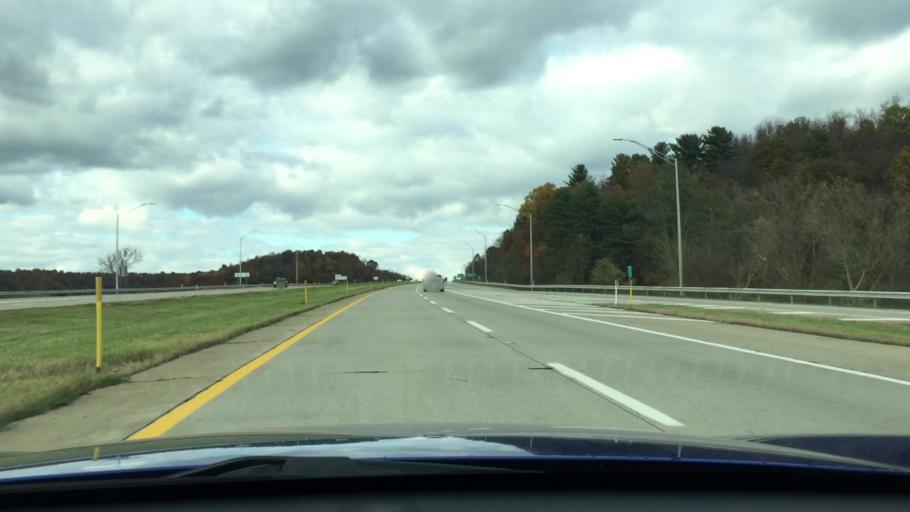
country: US
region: Pennsylvania
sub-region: Westmoreland County
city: New Stanton
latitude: 40.2380
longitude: -79.6048
